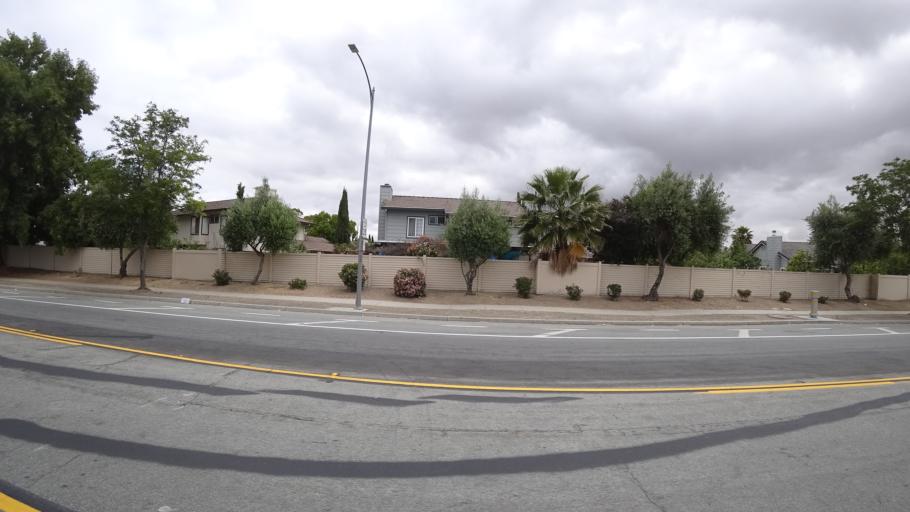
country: US
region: California
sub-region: Santa Clara County
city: Seven Trees
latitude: 37.2849
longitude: -121.8255
